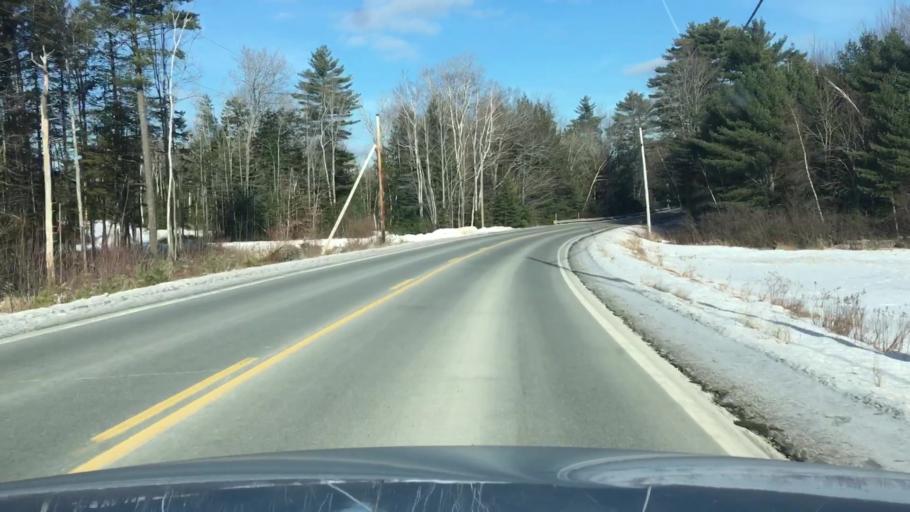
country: US
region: Maine
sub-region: Penobscot County
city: Holden
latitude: 44.7509
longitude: -68.6109
